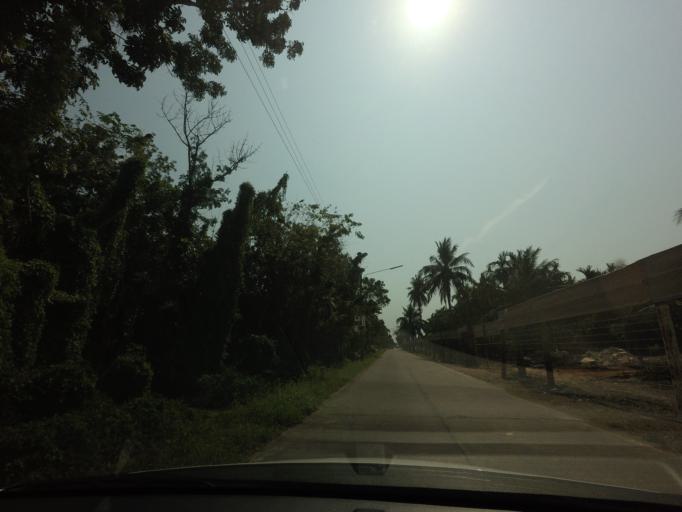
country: TH
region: Nakhon Pathom
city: Sam Phran
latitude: 13.7339
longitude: 100.2648
